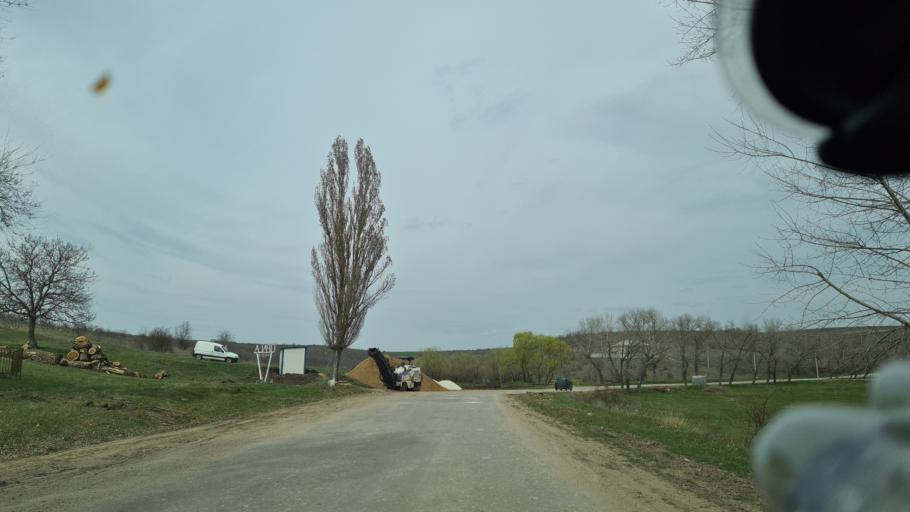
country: MD
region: Chisinau
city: Singera
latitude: 46.8404
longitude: 28.9794
